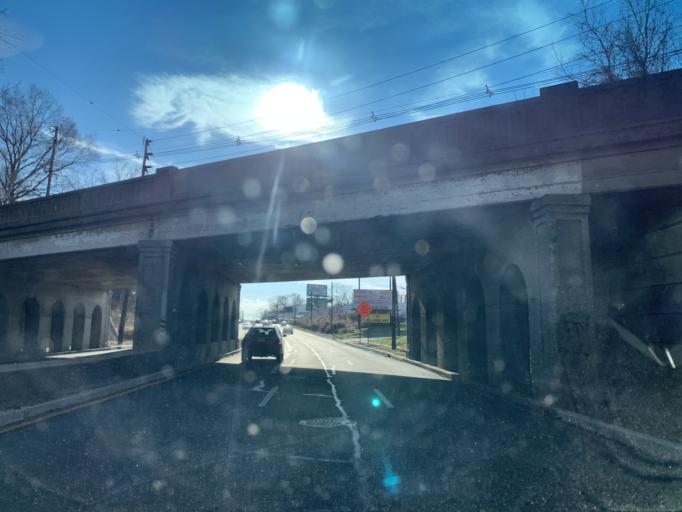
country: US
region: New Jersey
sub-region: Camden County
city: Wood-Lynne
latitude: 39.9111
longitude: -75.0934
